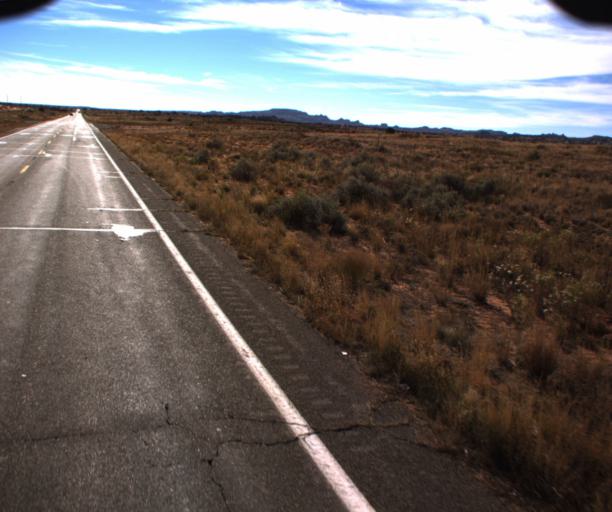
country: US
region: Arizona
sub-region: Coconino County
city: Kaibito
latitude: 36.6105
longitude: -111.1846
